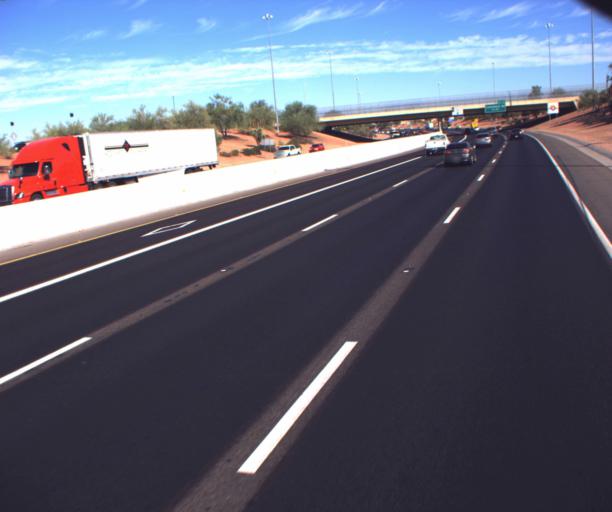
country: US
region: Arizona
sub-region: Maricopa County
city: Tolleson
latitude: 33.4923
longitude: -112.2637
